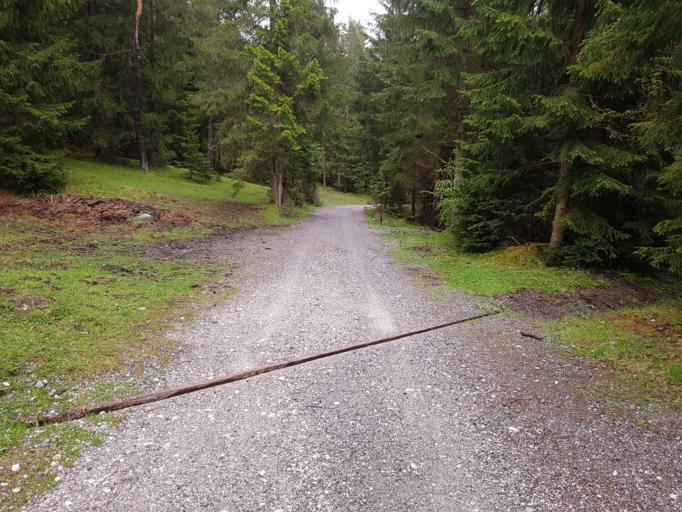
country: AT
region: Tyrol
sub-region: Politischer Bezirk Imst
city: Obsteig
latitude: 47.3062
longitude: 10.9148
